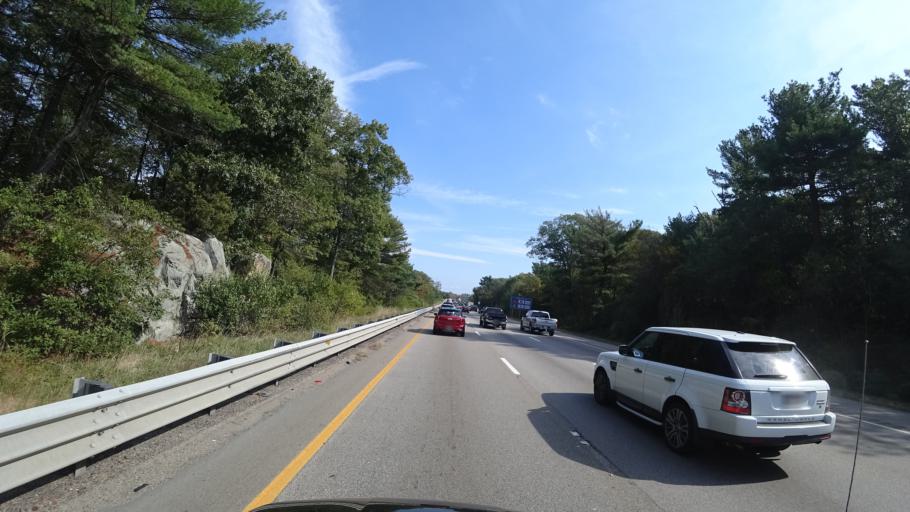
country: US
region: Massachusetts
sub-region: Norfolk County
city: Weymouth
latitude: 42.1880
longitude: -70.9376
